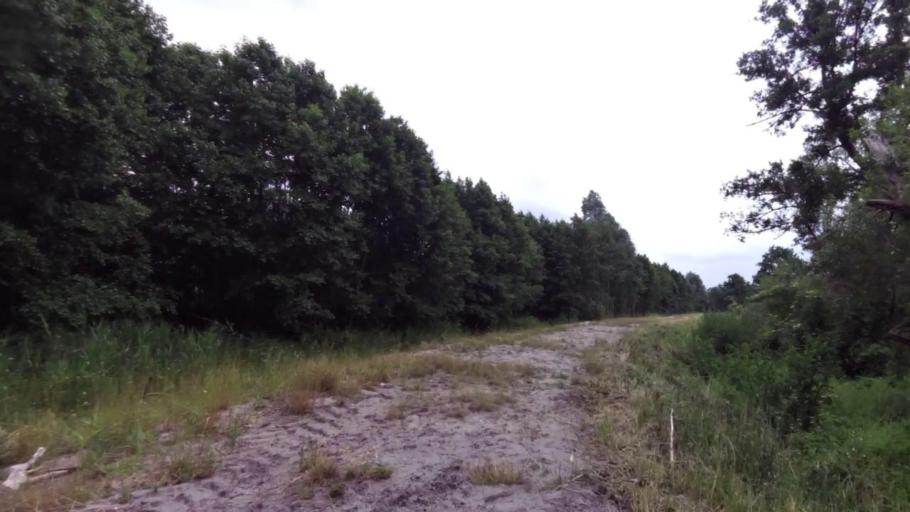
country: PL
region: West Pomeranian Voivodeship
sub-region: Szczecin
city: Szczecin
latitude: 53.4153
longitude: 14.6634
